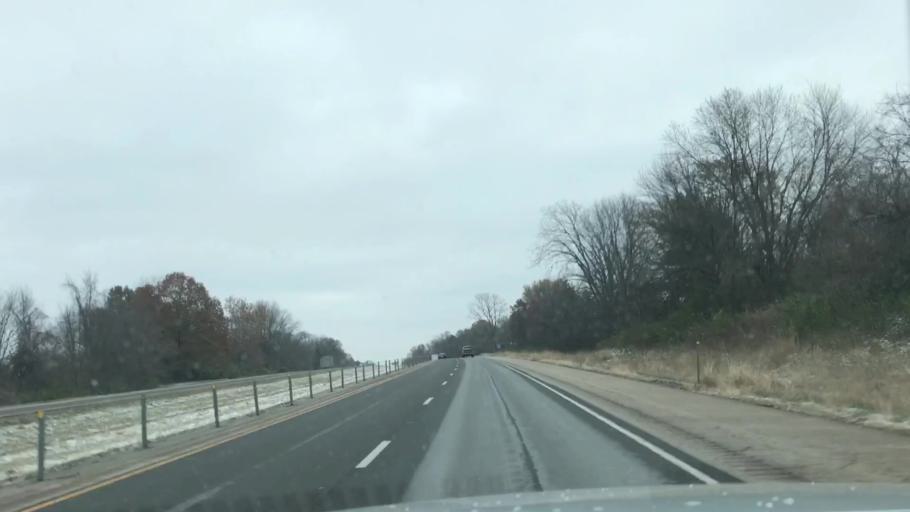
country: US
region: Illinois
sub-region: Madison County
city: Maryville
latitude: 38.7539
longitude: -89.9488
